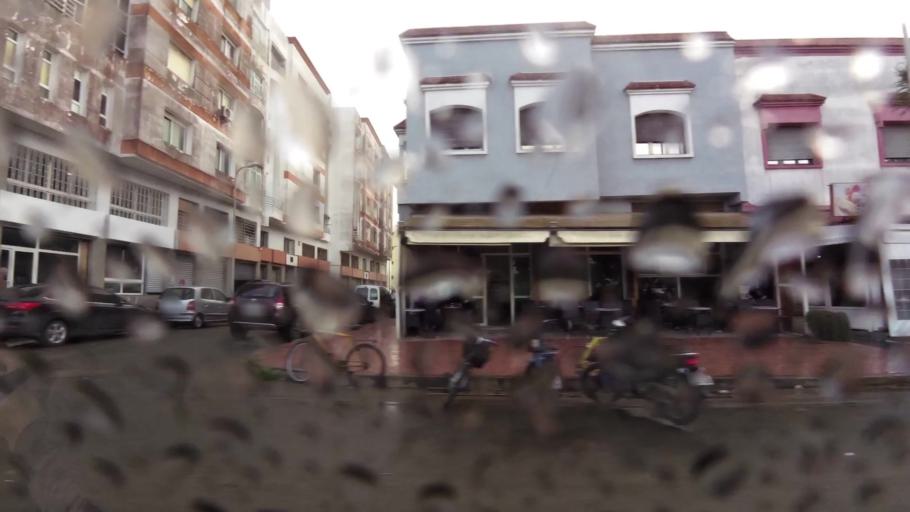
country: MA
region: Doukkala-Abda
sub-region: El-Jadida
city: El Jadida
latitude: 33.2440
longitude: -8.5229
